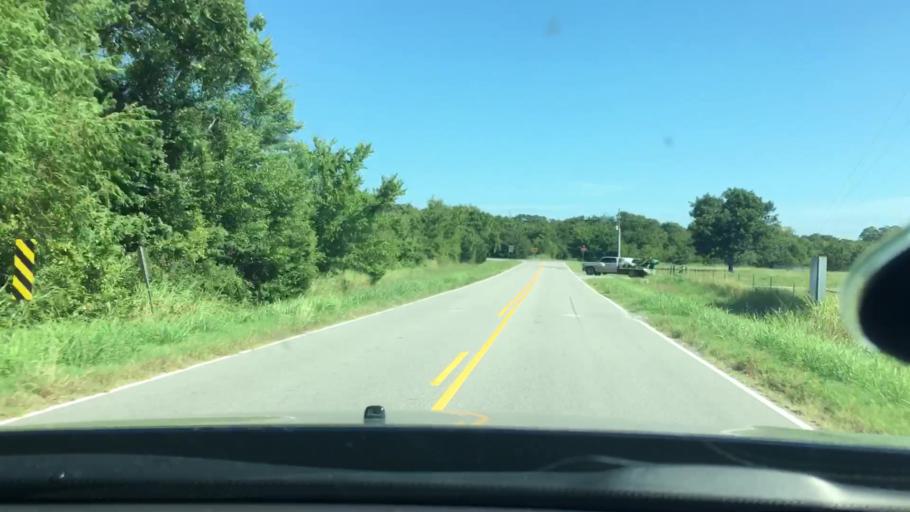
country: US
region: Oklahoma
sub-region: Johnston County
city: Tishomingo
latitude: 34.3597
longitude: -96.5488
